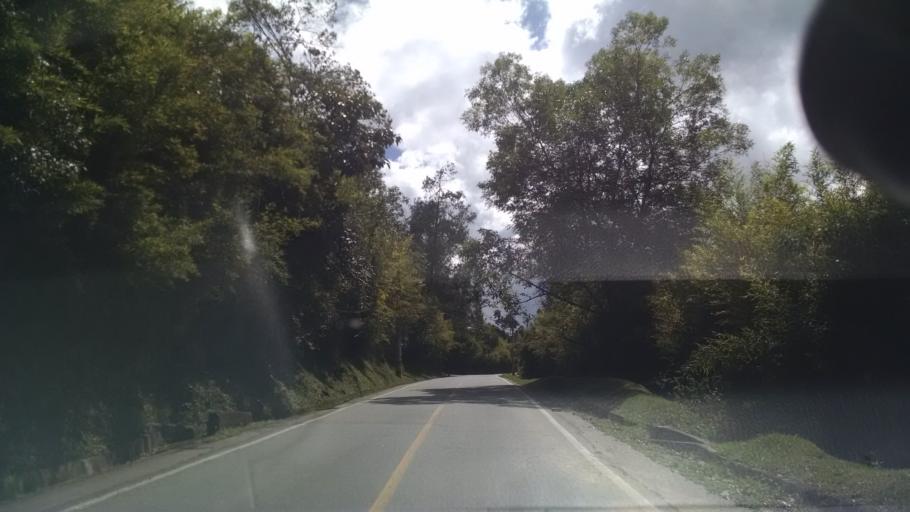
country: CO
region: Antioquia
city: El Retiro
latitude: 6.0907
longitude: -75.5018
